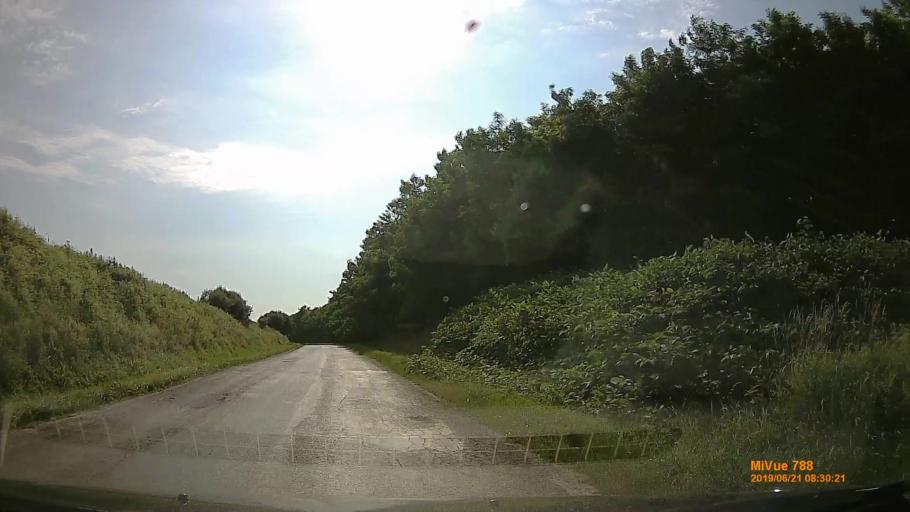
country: HU
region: Baranya
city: Szigetvar
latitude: 46.1470
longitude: 17.8569
